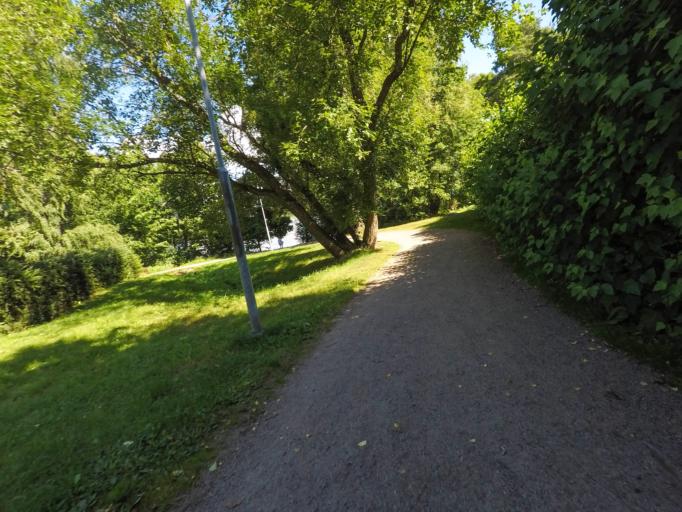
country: FI
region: Uusimaa
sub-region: Helsinki
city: Vantaa
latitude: 60.1950
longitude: 25.0680
